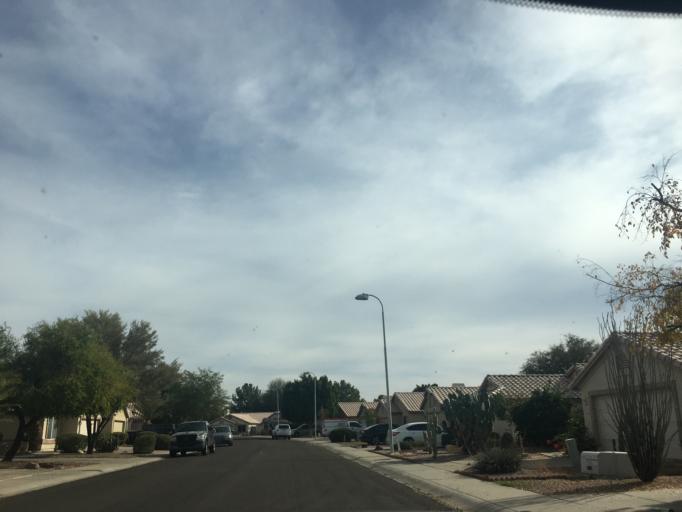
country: US
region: Arizona
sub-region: Maricopa County
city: Gilbert
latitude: 33.3483
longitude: -111.8092
